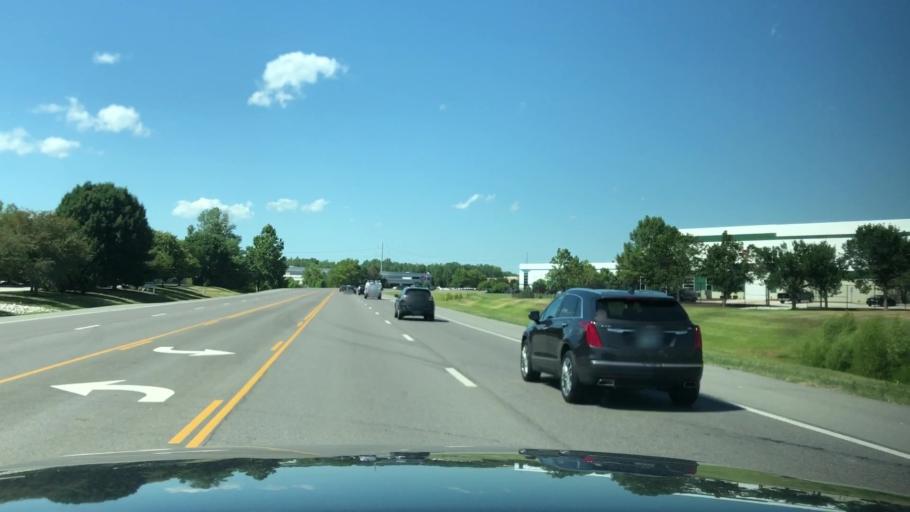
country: US
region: Missouri
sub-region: Saint Charles County
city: Saint Charles
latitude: 38.7828
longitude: -90.4590
